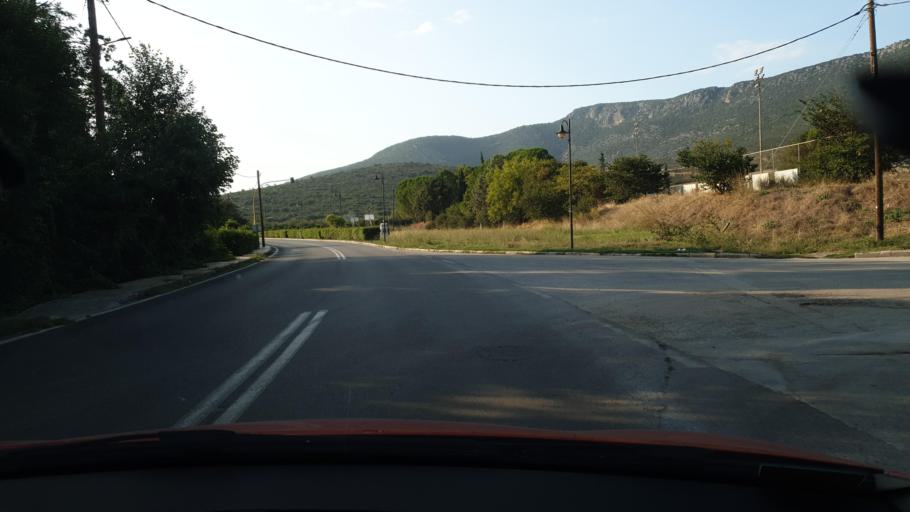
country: GR
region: Thessaly
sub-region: Nomos Magnisias
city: Sourpi
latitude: 39.1070
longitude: 22.8915
